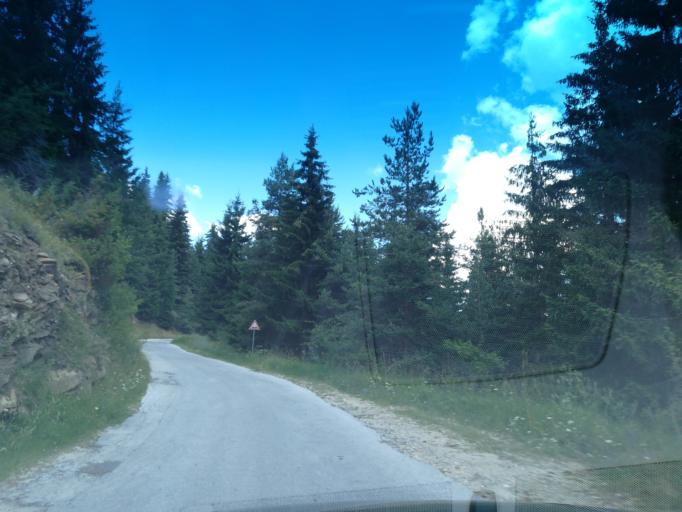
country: BG
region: Smolyan
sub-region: Obshtina Chepelare
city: Chepelare
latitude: 41.6769
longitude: 24.7703
